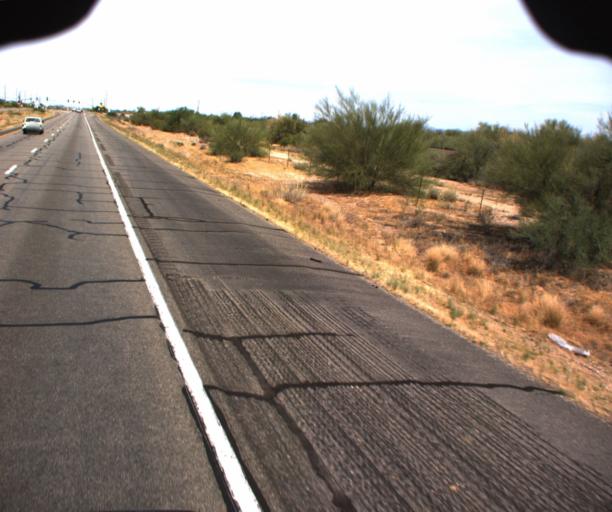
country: US
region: Arizona
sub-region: Maricopa County
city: Sun City West
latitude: 33.7758
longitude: -112.5257
